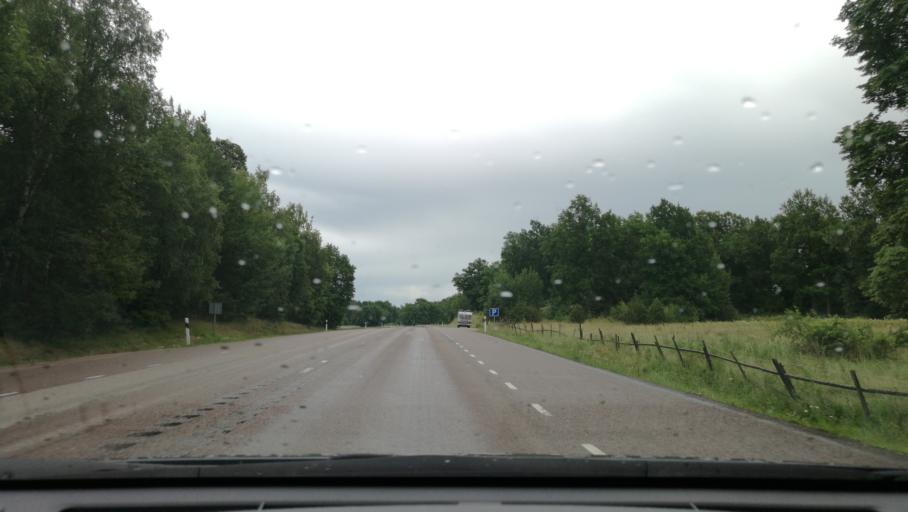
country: SE
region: Vaestmanland
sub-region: Kungsors Kommun
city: Kungsoer
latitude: 59.4356
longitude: 16.0617
